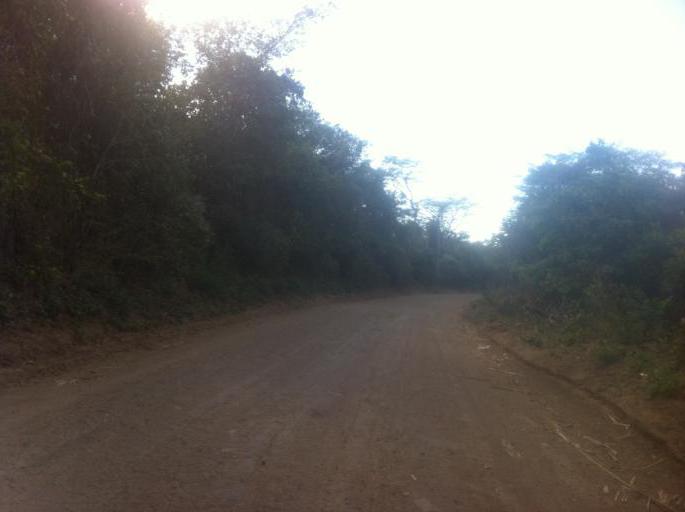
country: NI
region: Managua
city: Masachapa
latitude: 11.8294
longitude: -86.5056
